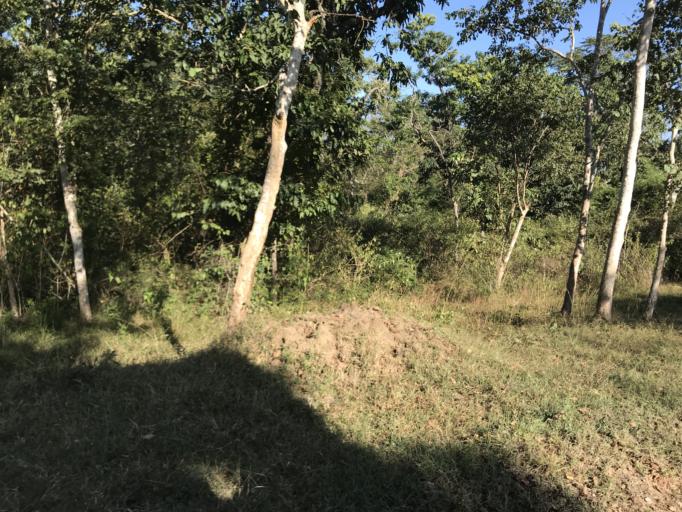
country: IN
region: Karnataka
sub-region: Mysore
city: Heggadadevankote
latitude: 11.9773
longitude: 76.2395
